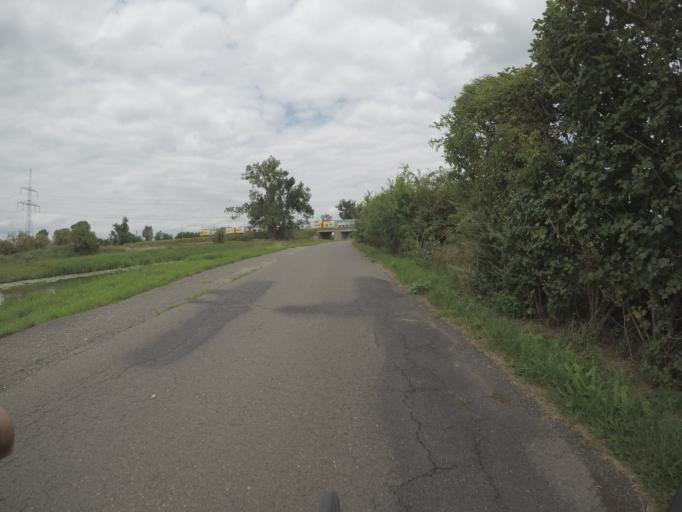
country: DE
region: Brandenburg
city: Wustermark
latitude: 52.5985
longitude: 12.9349
